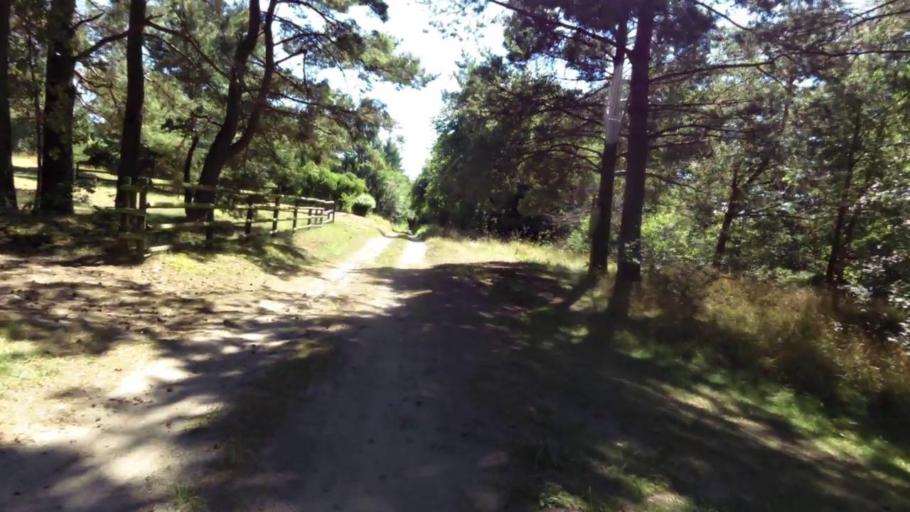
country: PL
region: West Pomeranian Voivodeship
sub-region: Powiat szczecinecki
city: Bialy Bor
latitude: 53.8372
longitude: 16.8744
